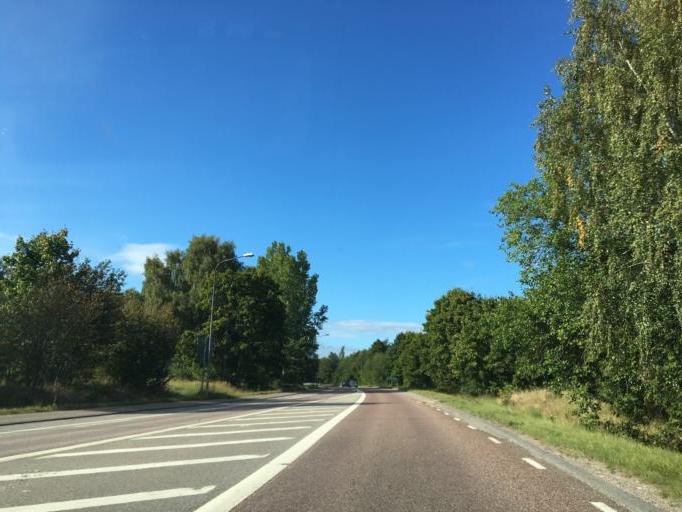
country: SE
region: Soedermanland
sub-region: Nykopings Kommun
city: Nykoping
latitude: 58.7732
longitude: 16.9834
